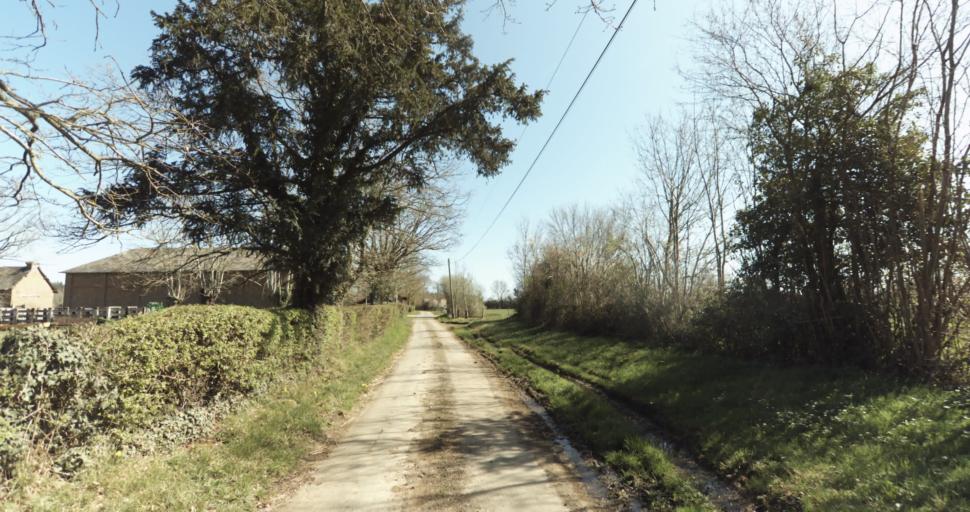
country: FR
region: Lower Normandy
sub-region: Departement du Calvados
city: Livarot
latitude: 49.0196
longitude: 0.0919
